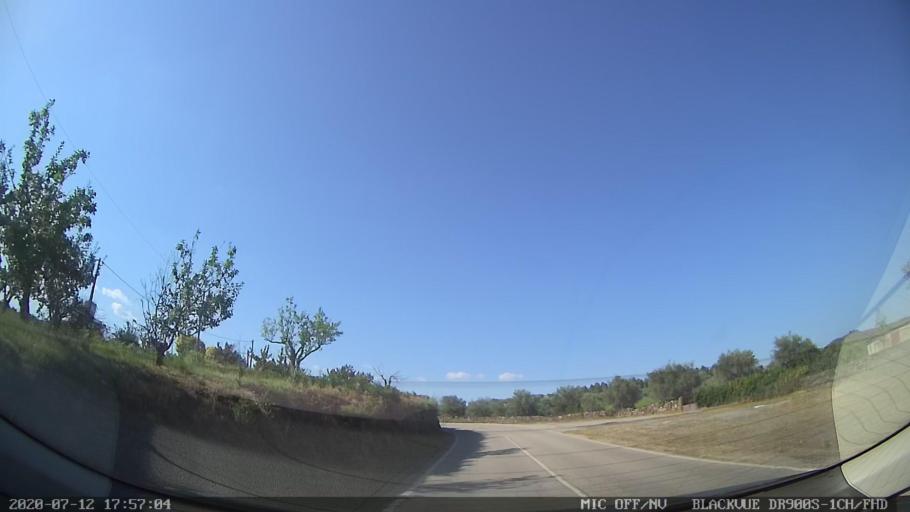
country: PT
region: Vila Real
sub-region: Sabrosa
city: Sabrosa
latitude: 41.2735
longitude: -7.4604
